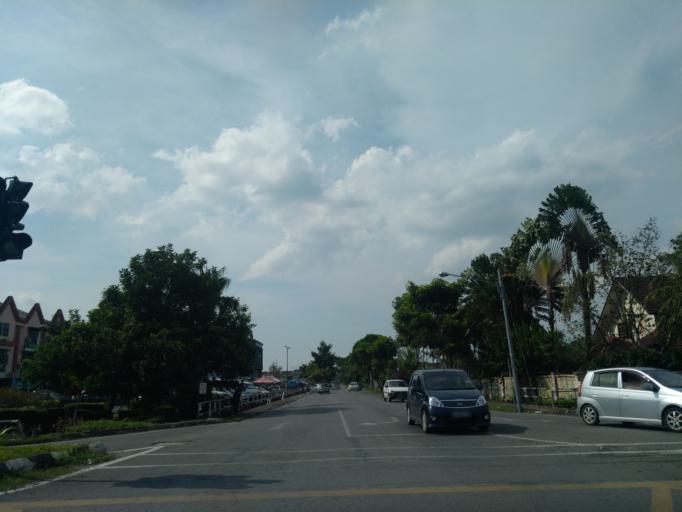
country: MY
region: Sarawak
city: Kuching
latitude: 1.5733
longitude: 110.2980
